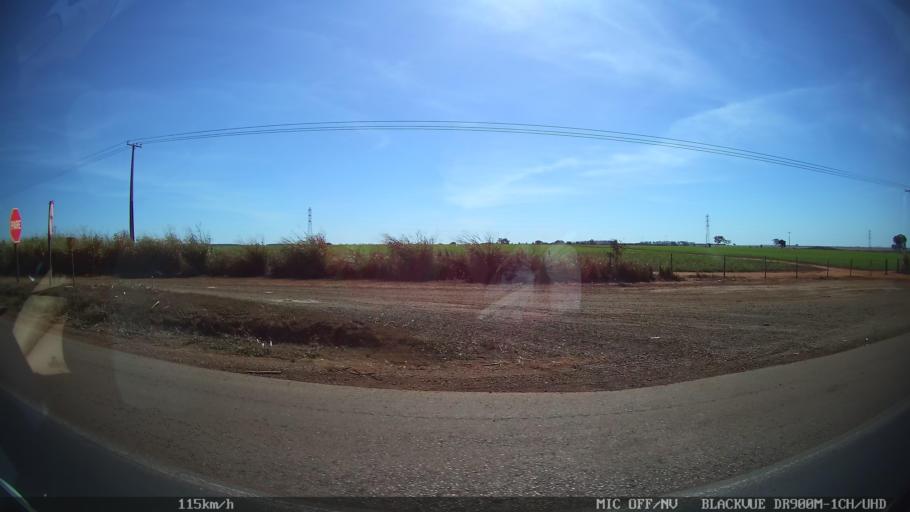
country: BR
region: Sao Paulo
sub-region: Barretos
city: Barretos
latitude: -20.4772
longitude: -48.4972
